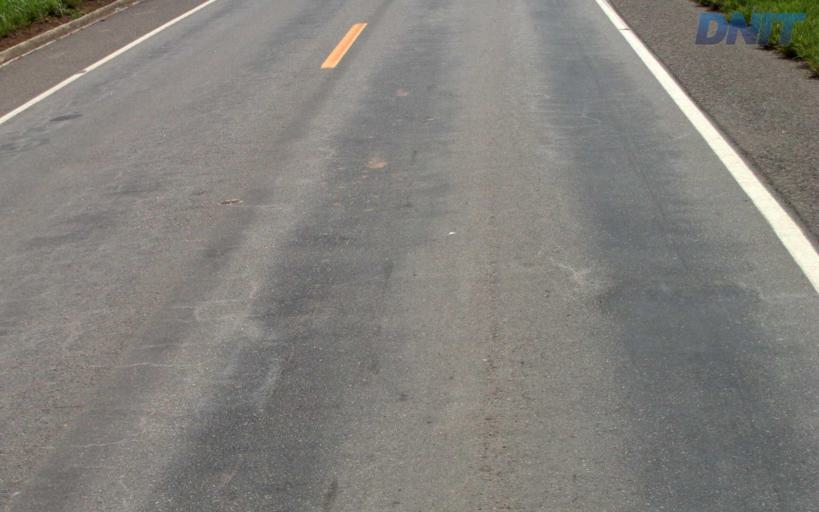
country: BR
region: Minas Gerais
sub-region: Governador Valadares
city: Governador Valadares
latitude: -18.9846
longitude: -42.1071
